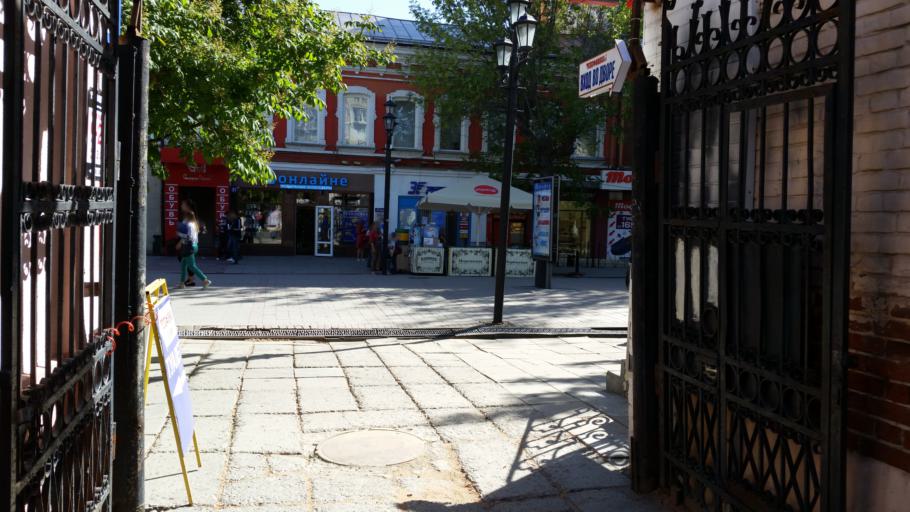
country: RU
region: Saratov
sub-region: Saratovskiy Rayon
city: Saratov
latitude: 51.5322
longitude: 46.0252
